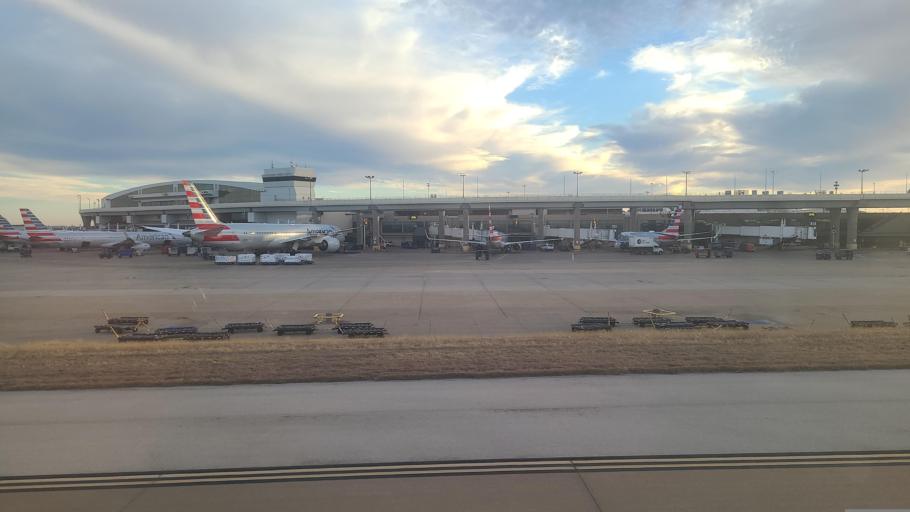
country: US
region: Texas
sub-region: Tarrant County
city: Grapevine
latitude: 32.9090
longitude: -97.0373
